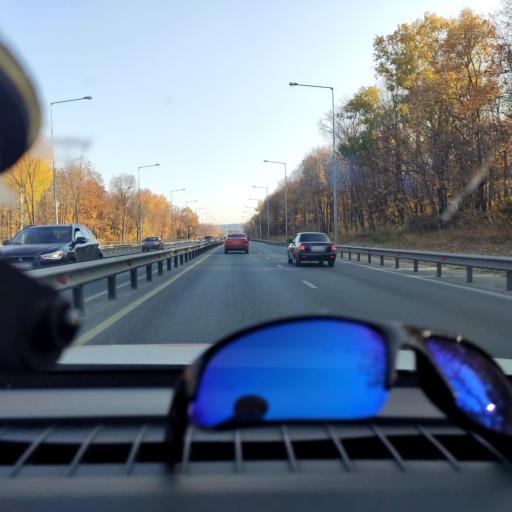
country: RU
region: Samara
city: Volzhskiy
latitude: 53.3620
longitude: 50.2034
